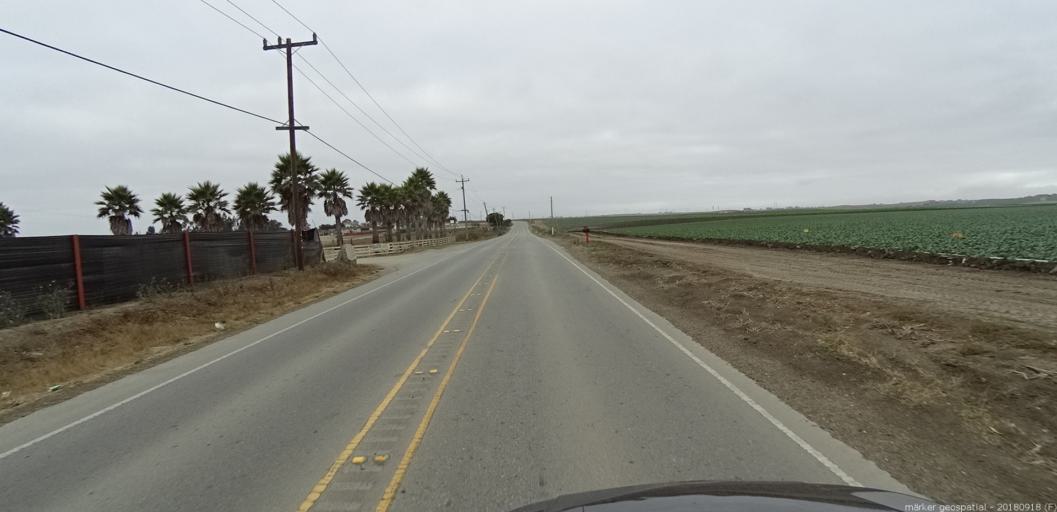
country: US
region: California
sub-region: Monterey County
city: Prunedale
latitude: 36.7471
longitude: -121.7002
